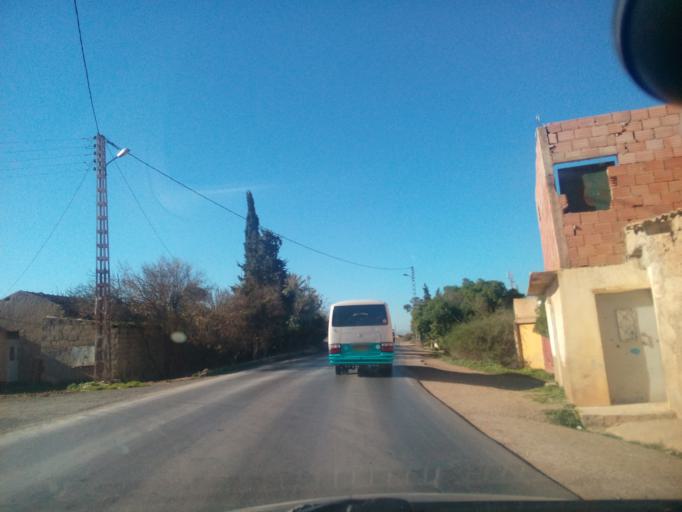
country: DZ
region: Relizane
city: Djidiouia
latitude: 35.8935
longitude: 0.7227
